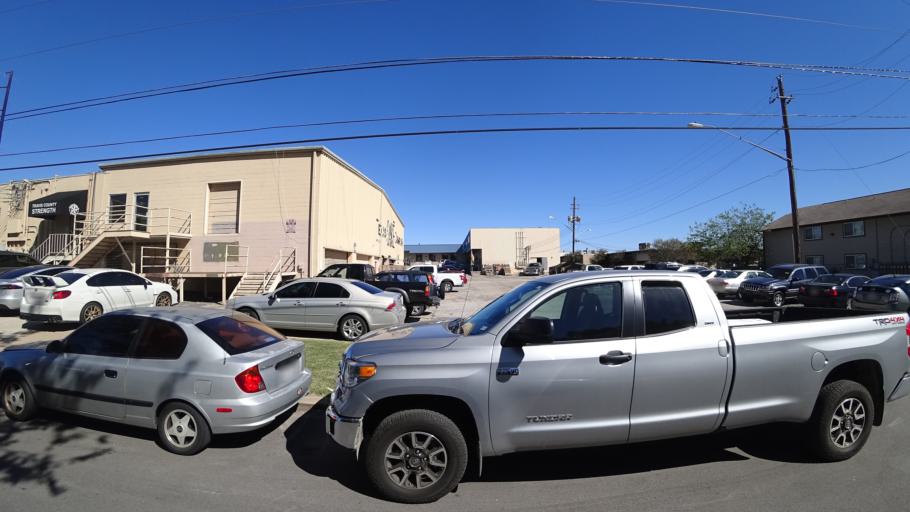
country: US
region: Texas
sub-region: Travis County
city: Austin
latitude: 30.3226
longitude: -97.7275
